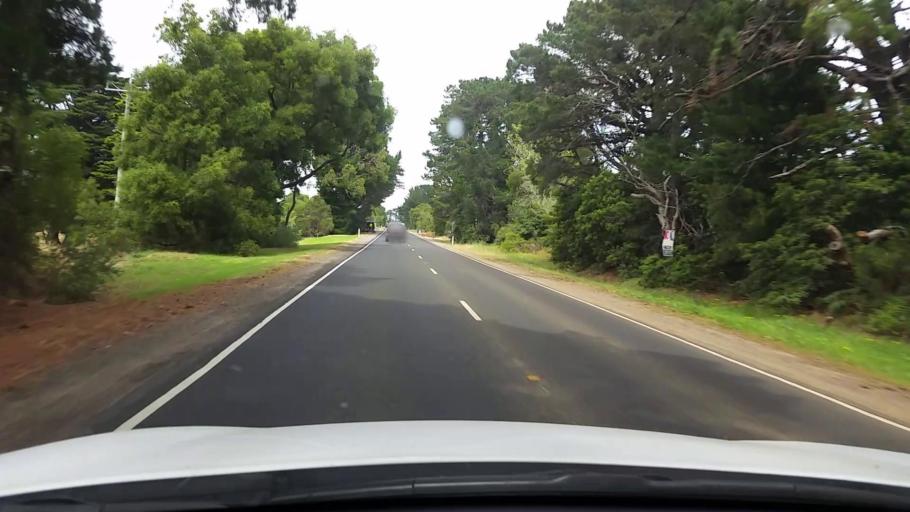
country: AU
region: Victoria
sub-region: Mornington Peninsula
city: Merricks
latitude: -38.4099
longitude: 145.0607
